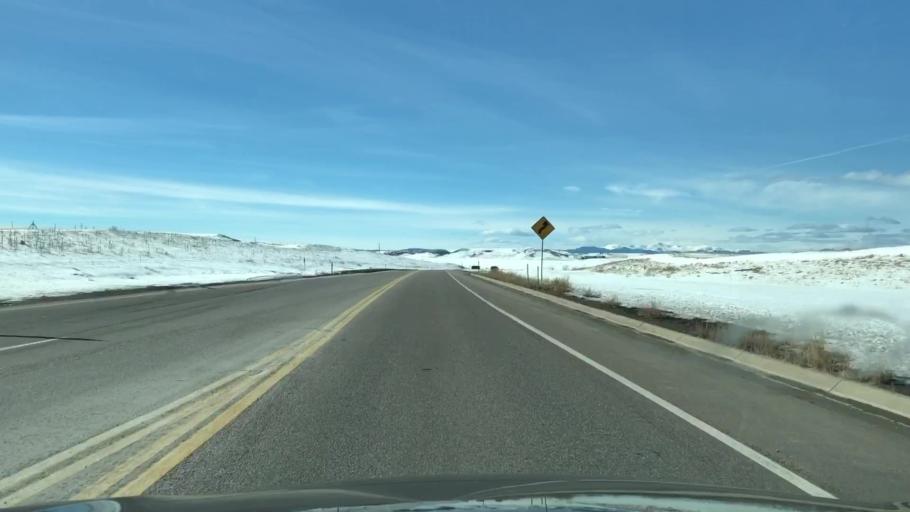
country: US
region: Colorado
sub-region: Douglas County
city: Stonegate
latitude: 39.5223
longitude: -104.8303
